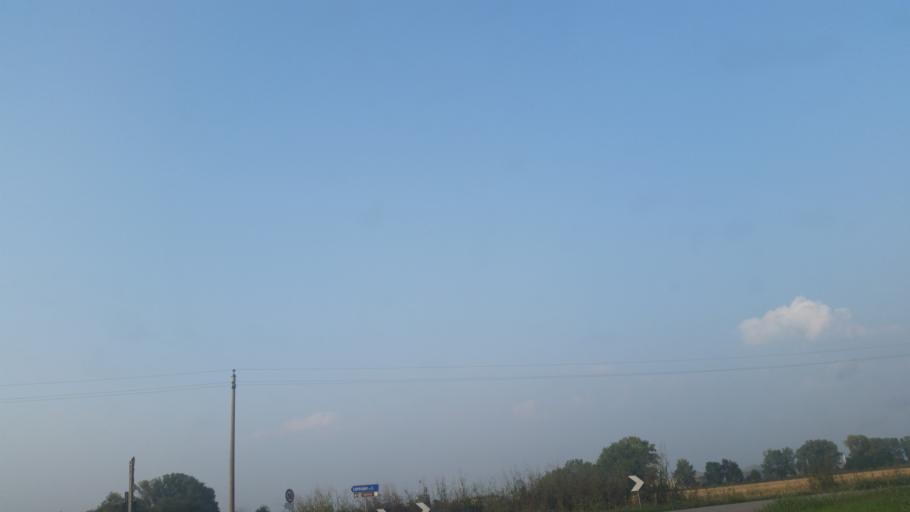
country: IT
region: Lombardy
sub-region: Provincia di Brescia
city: Azzano Mella
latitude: 45.4262
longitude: 10.1288
